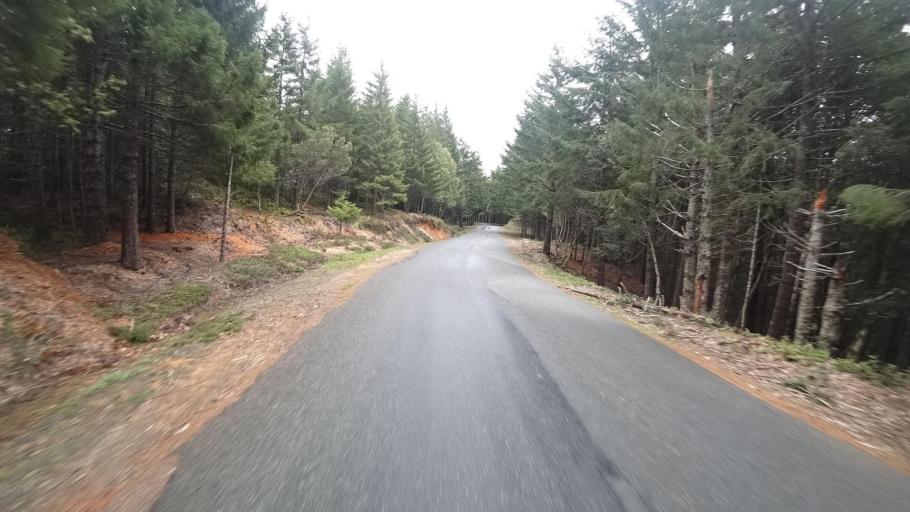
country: US
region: California
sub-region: Humboldt County
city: Willow Creek
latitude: 41.2023
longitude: -123.7980
